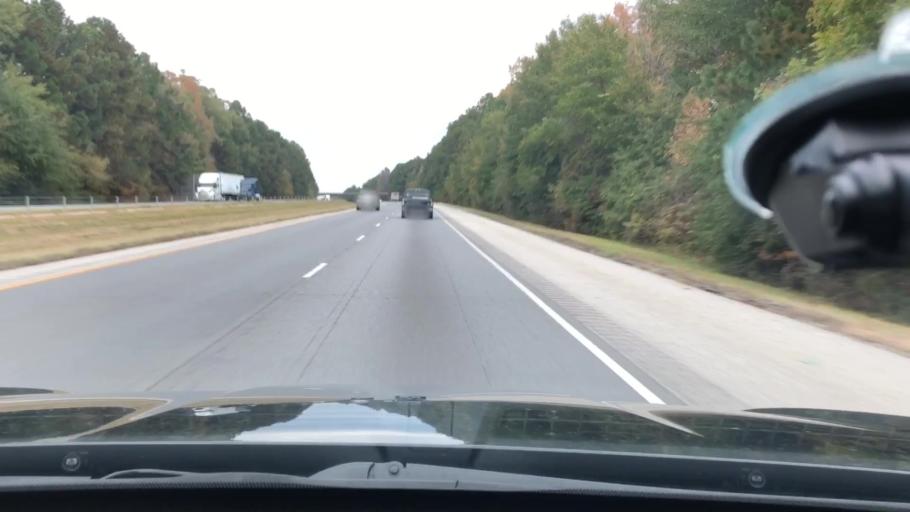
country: US
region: Arkansas
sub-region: Clark County
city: Arkadelphia
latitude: 34.1379
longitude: -93.0824
